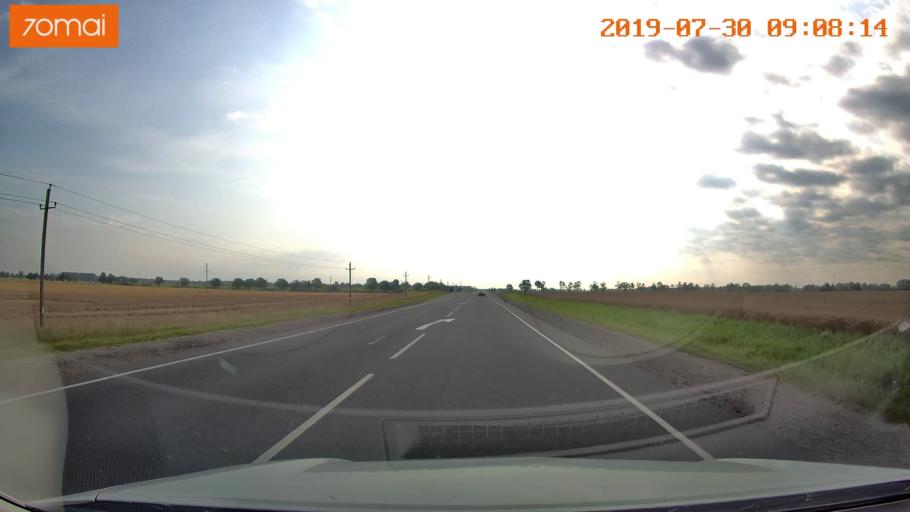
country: RU
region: Kaliningrad
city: Gusev
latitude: 54.6124
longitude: 22.3809
